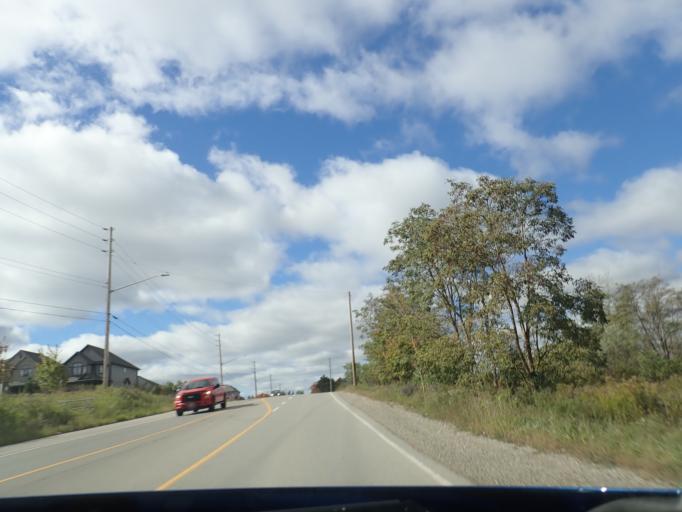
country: CA
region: Ontario
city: London
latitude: 43.0439
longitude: -81.2701
